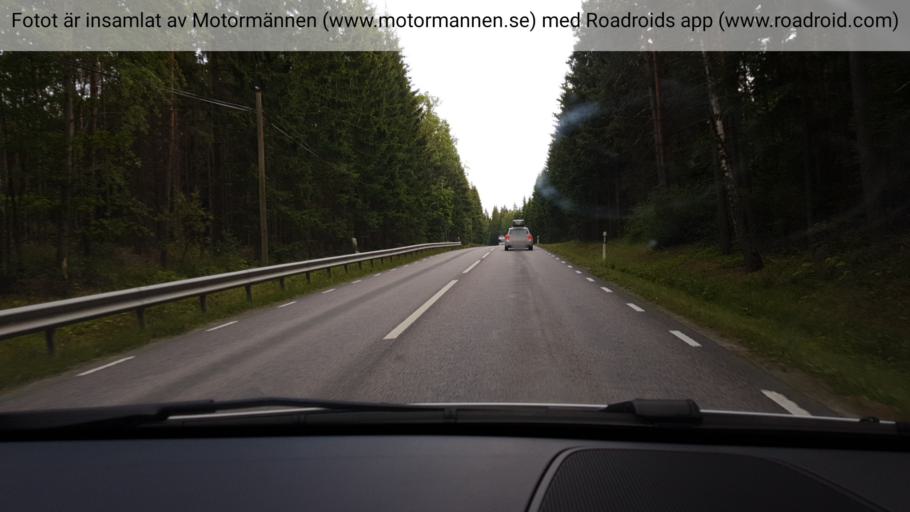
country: SE
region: Stockholm
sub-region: Sigtuna Kommun
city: Sigtuna
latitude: 59.6446
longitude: 17.7032
